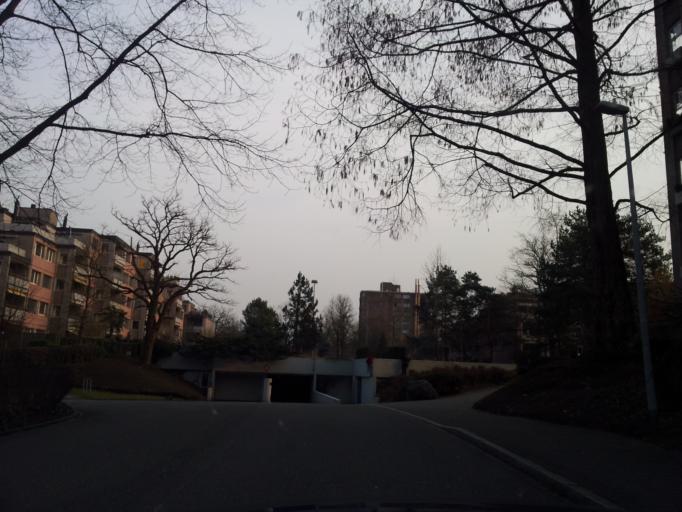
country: CH
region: Zug
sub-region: Zug
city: Cham
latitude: 47.1870
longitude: 8.4511
